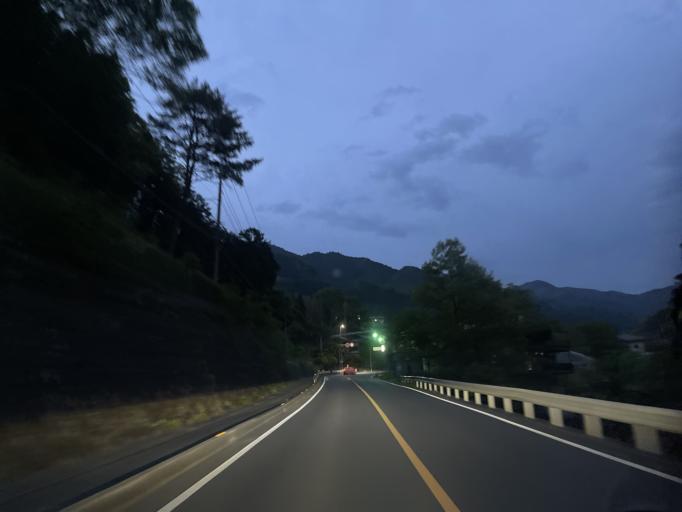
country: JP
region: Saitama
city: Chichibu
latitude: 35.9777
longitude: 139.1317
